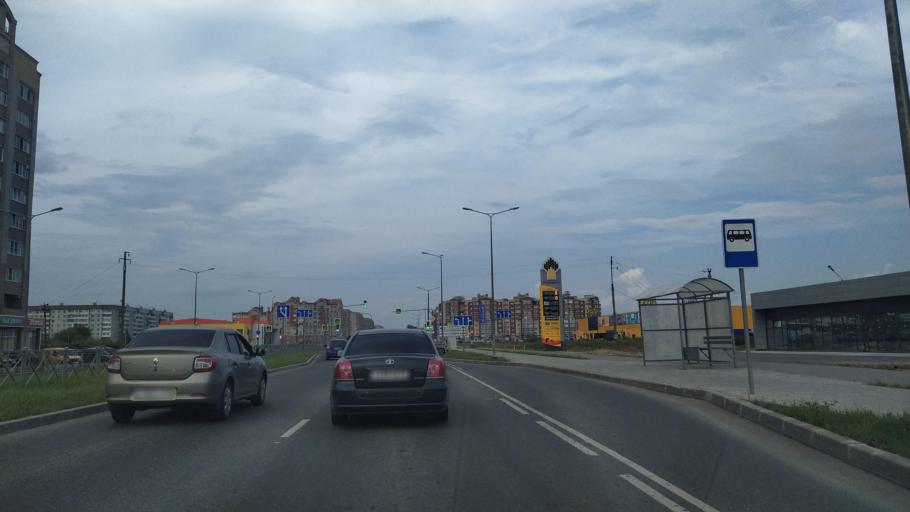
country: RU
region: Novgorod
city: Pankovka
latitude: 58.5045
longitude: 31.2262
